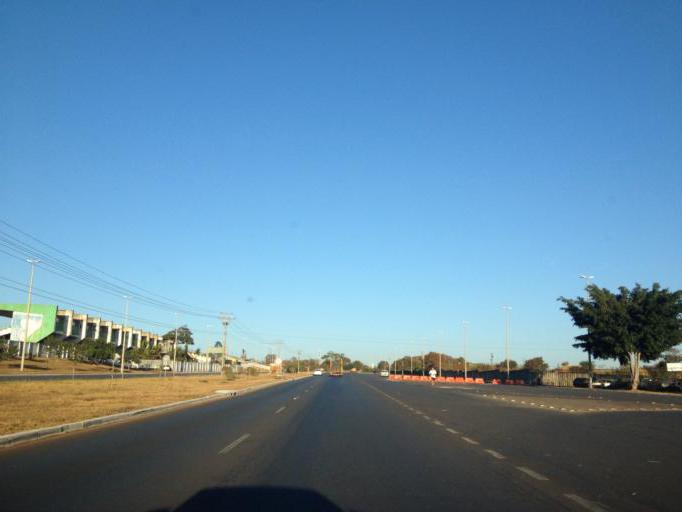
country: BR
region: Federal District
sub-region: Brasilia
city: Brasilia
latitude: -15.7712
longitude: -47.8985
